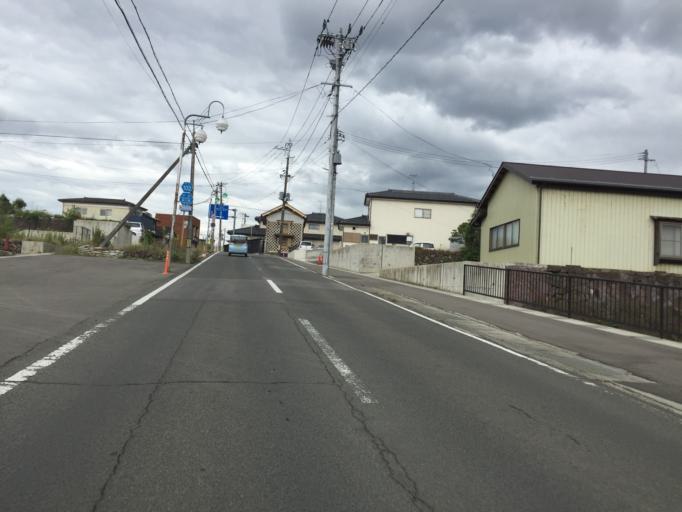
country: JP
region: Fukushima
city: Yanagawamachi-saiwaicho
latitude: 37.8600
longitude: 140.6089
